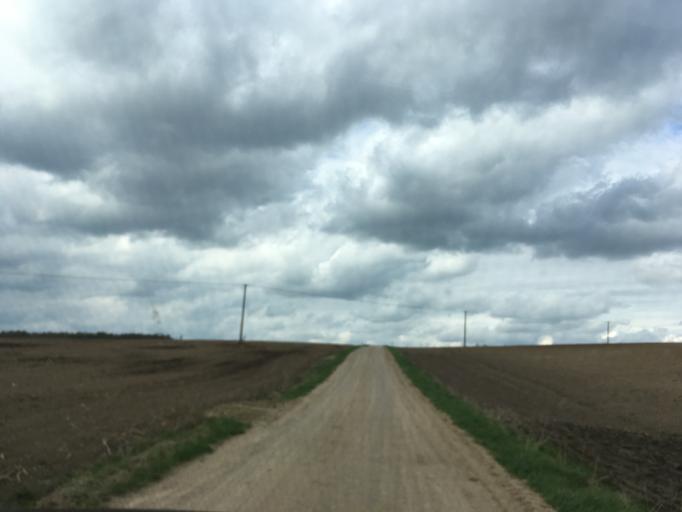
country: PL
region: Podlasie
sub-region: Powiat sejnenski
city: Punsk
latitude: 54.3836
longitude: 22.9641
